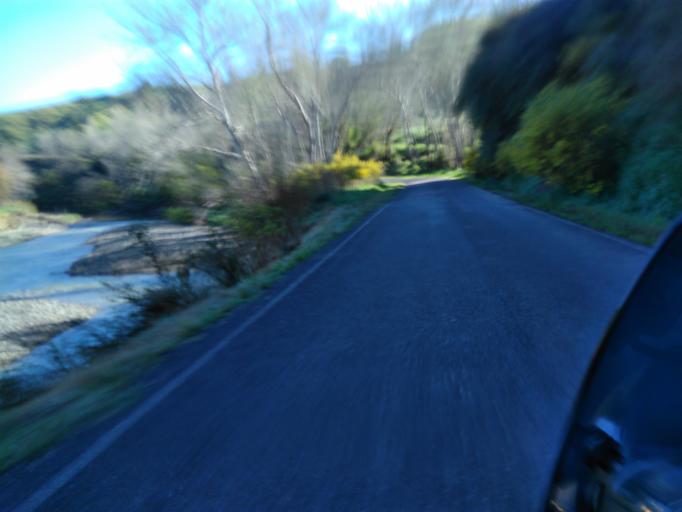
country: NZ
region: Gisborne
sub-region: Gisborne District
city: Gisborne
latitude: -38.4344
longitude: 177.7430
